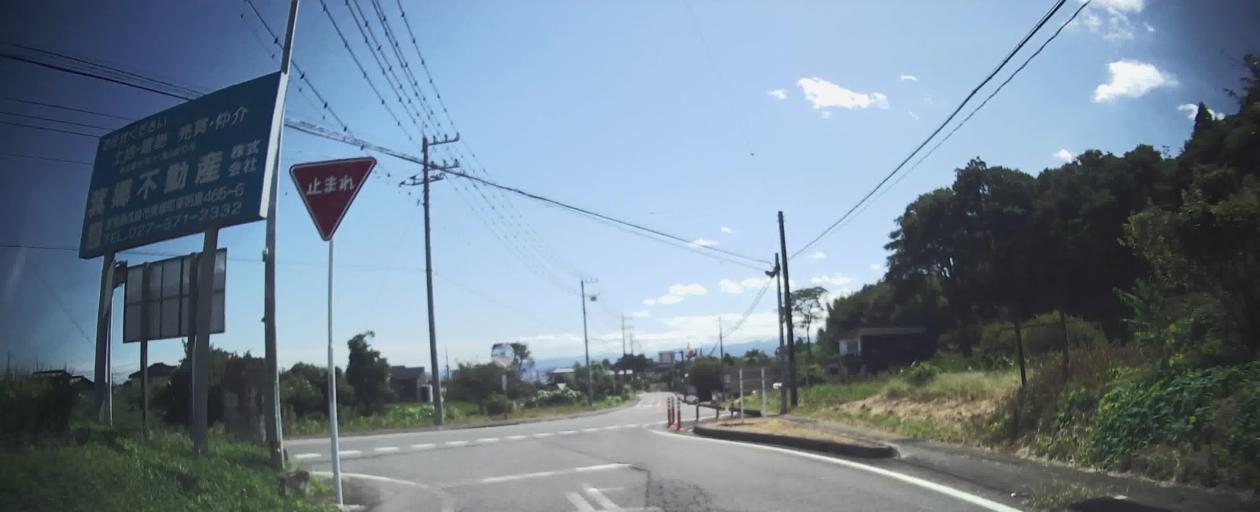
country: JP
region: Gunma
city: Kanekomachi
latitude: 36.4028
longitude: 138.9558
